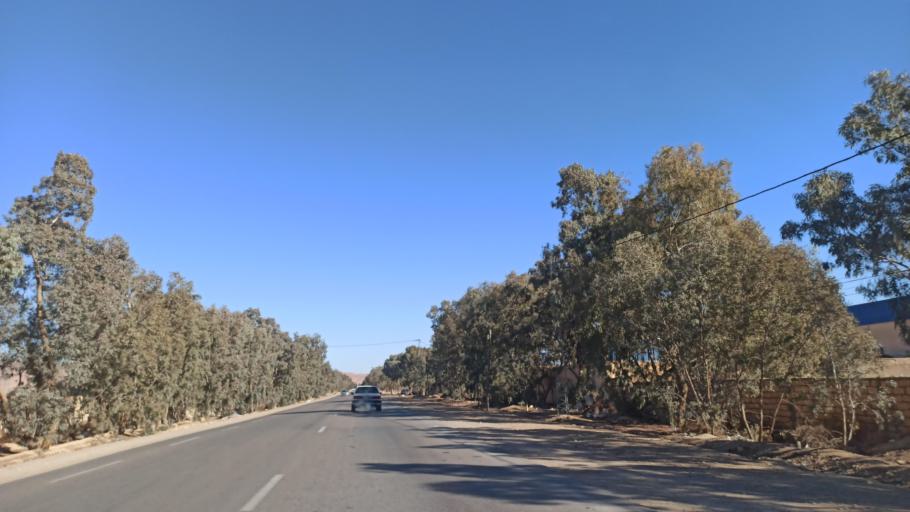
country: TN
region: Gafsa
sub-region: Gafsa Municipality
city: Gafsa
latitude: 34.3937
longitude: 8.7151
